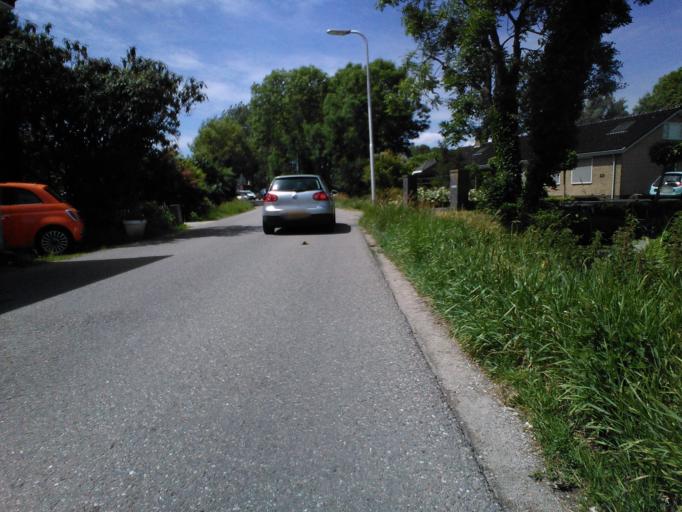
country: NL
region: South Holland
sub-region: Gemeente Papendrecht
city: Papendrecht
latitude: 51.8574
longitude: 4.6986
